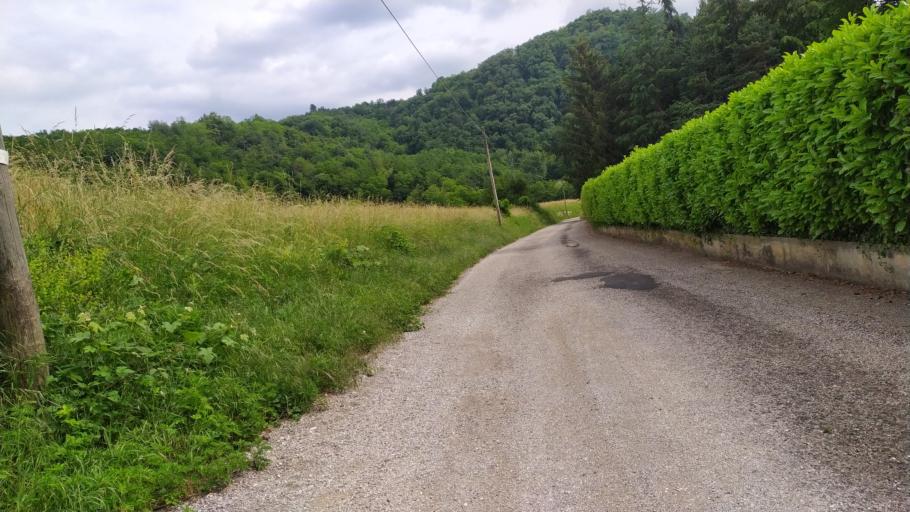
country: IT
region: Veneto
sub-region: Provincia di Vicenza
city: Schio
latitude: 45.6964
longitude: 11.3366
